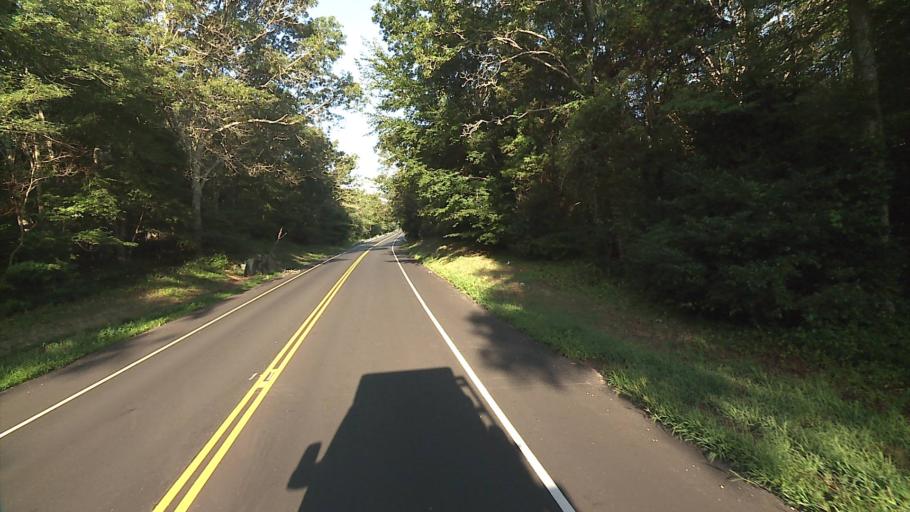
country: US
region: Connecticut
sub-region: New London County
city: Pawcatuck
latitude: 41.3506
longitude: -71.8964
